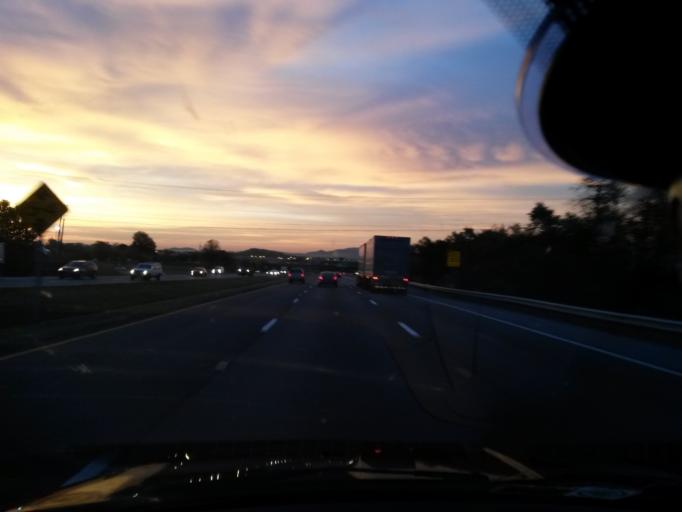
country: US
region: Virginia
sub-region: Roanoke County
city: Hollins
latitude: 37.3298
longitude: -79.9919
